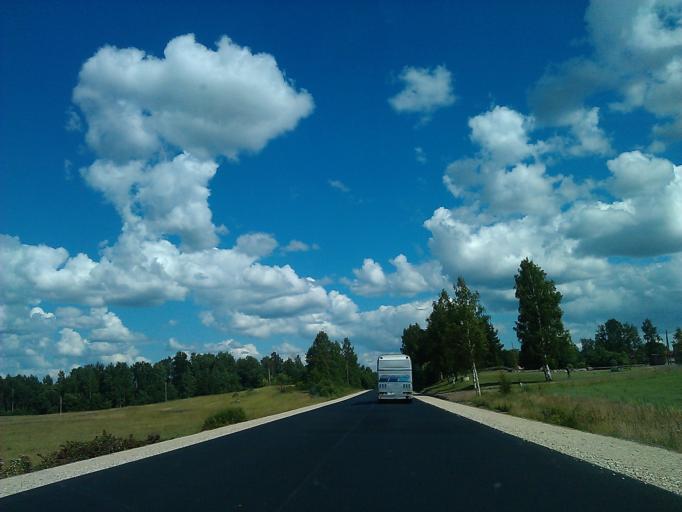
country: LV
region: Rezekne
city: Rezekne
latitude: 56.5428
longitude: 27.1355
